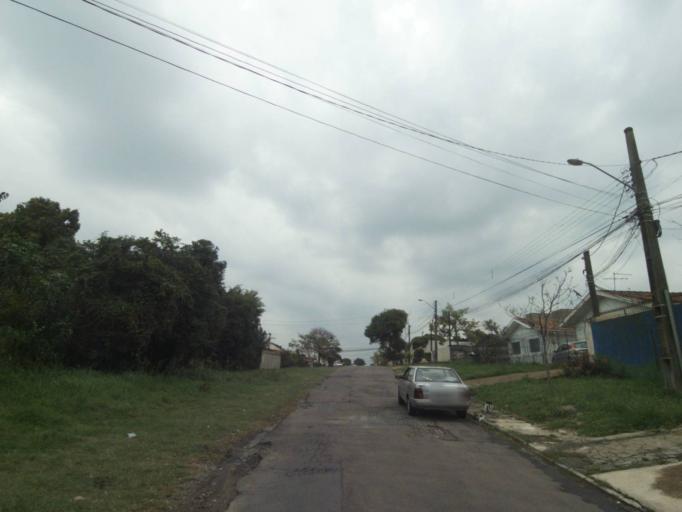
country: BR
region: Parana
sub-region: Curitiba
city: Curitiba
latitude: -25.4824
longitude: -49.3072
